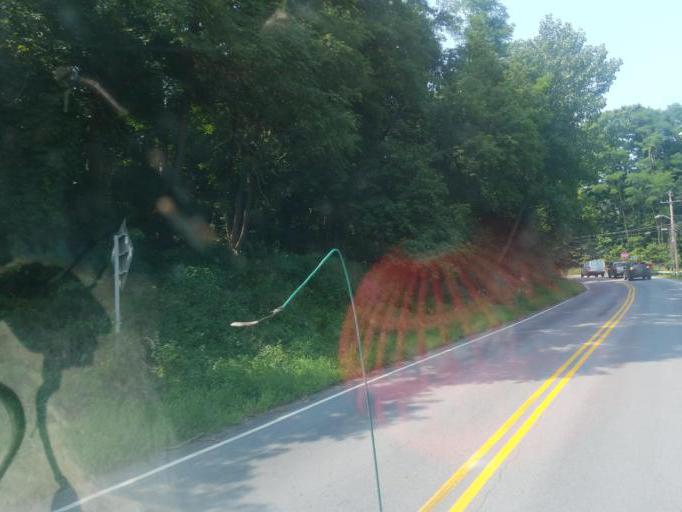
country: US
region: New York
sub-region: Montgomery County
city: Fonda
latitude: 42.9567
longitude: -74.3830
